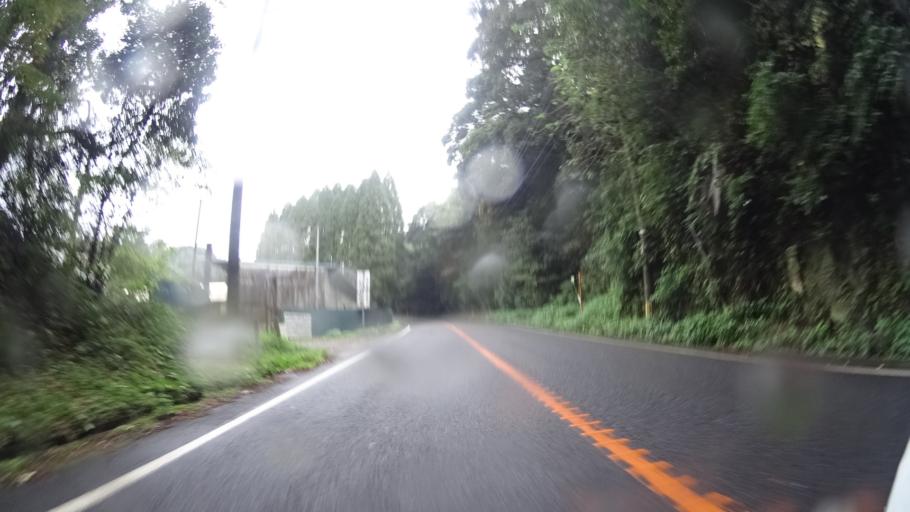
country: JP
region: Kagoshima
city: Kajiki
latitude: 31.7832
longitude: 130.6740
